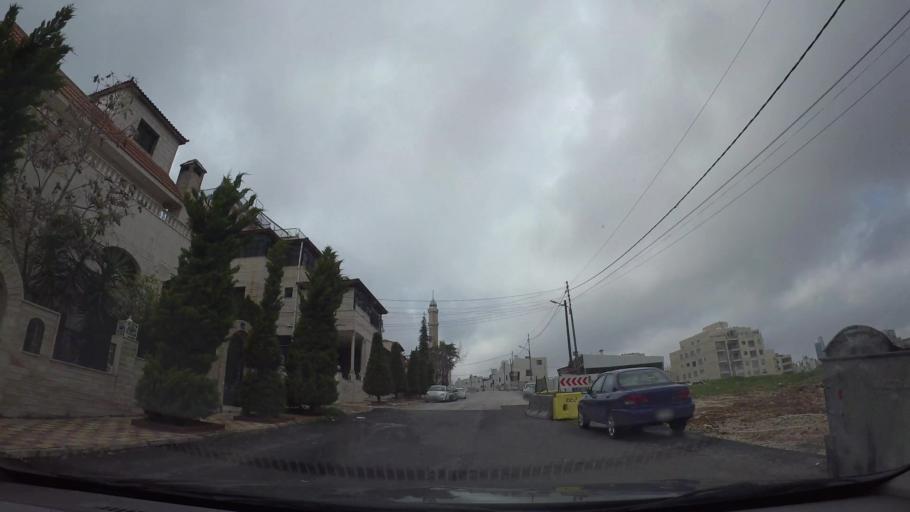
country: JO
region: Amman
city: Amman
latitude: 31.9416
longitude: 35.9048
